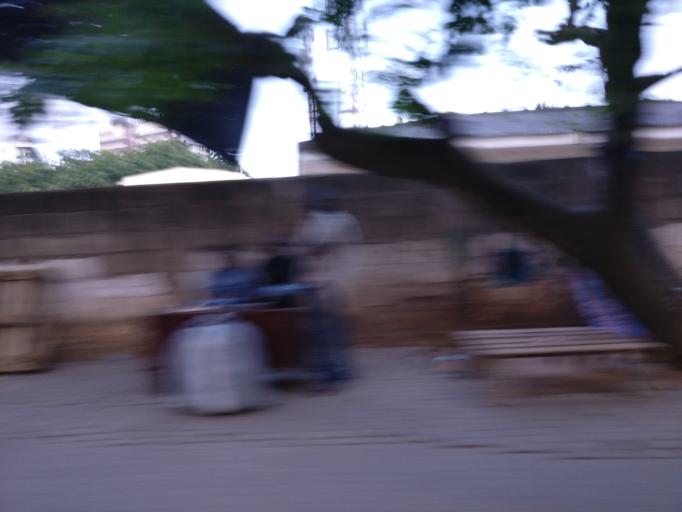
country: GH
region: Greater Accra
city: Accra
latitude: 5.5556
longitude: -0.2045
